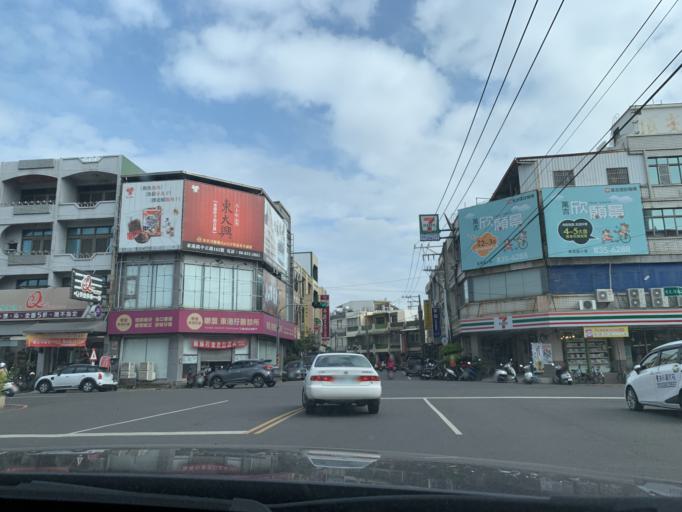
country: TW
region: Taiwan
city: Fengshan
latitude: 22.4673
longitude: 120.4531
